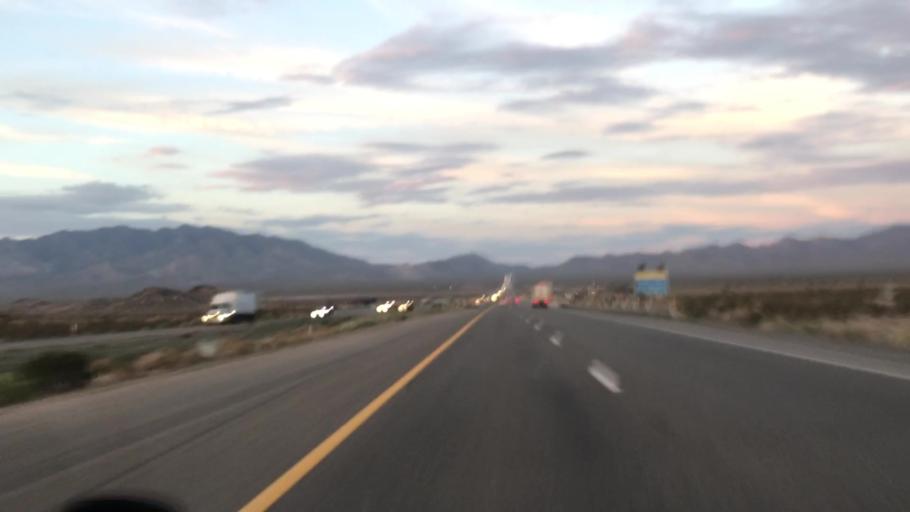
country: US
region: Nevada
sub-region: Clark County
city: Sandy Valley
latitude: 35.4312
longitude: -115.7104
